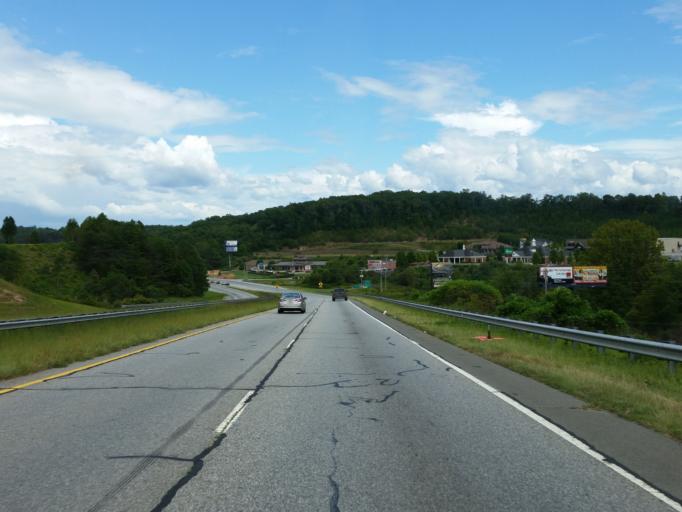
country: US
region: Georgia
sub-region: Fannin County
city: Blue Ridge
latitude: 34.8755
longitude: -84.3049
